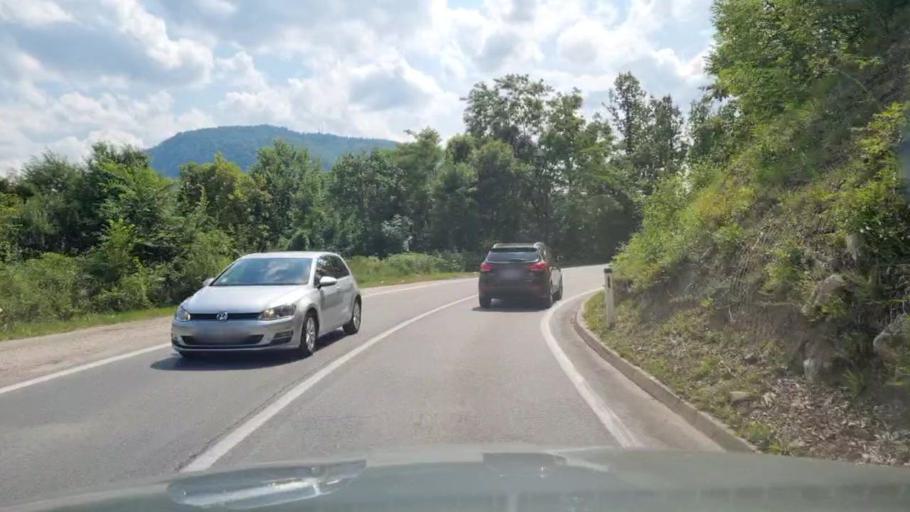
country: BA
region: Federation of Bosnia and Herzegovina
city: Kladanj
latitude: 44.2428
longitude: 18.7365
